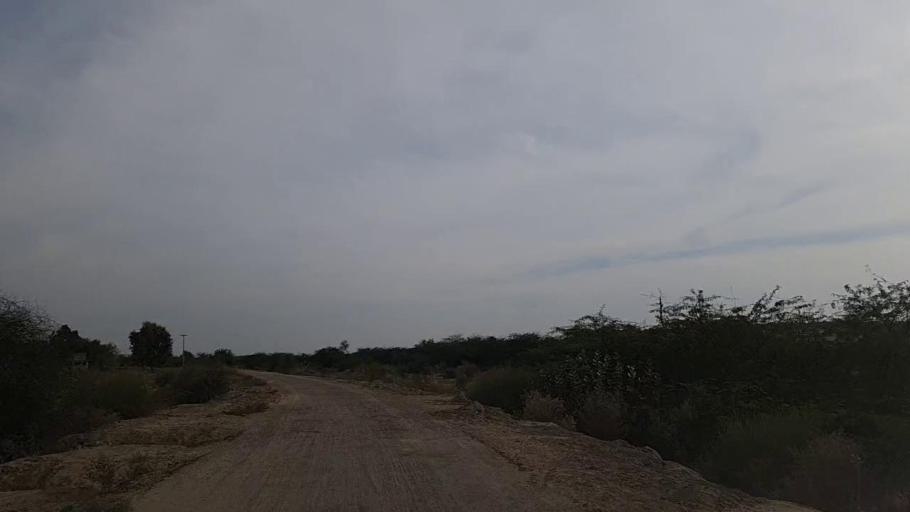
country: PK
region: Sindh
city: Jam Sahib
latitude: 26.4405
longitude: 68.6237
